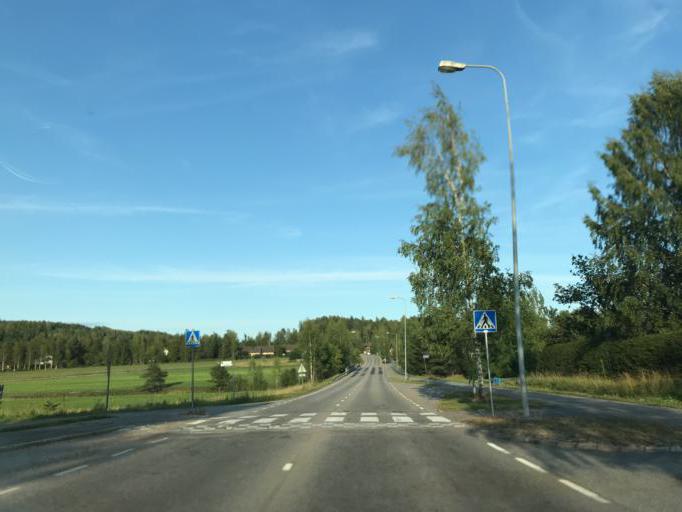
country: FI
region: Uusimaa
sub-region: Helsinki
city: Vihti
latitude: 60.4170
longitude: 24.3382
